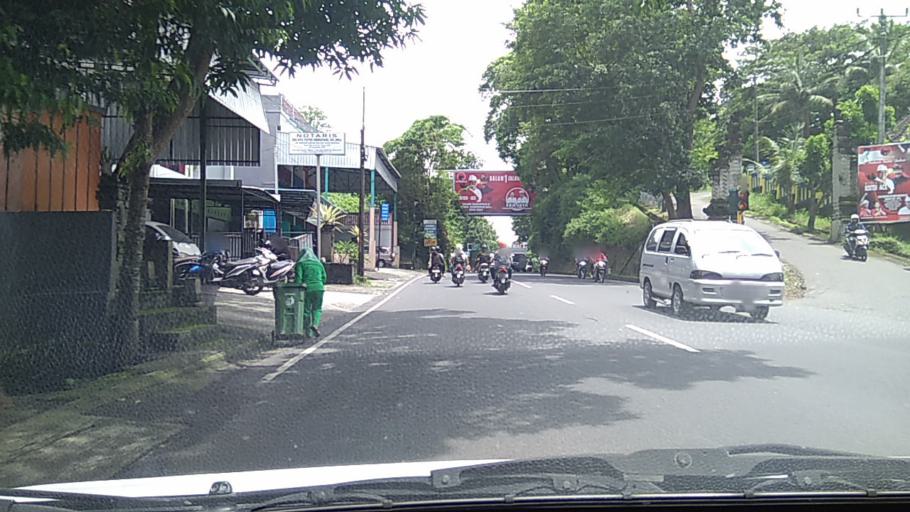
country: ID
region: Bali
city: Tabanan
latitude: -8.5424
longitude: 115.1385
